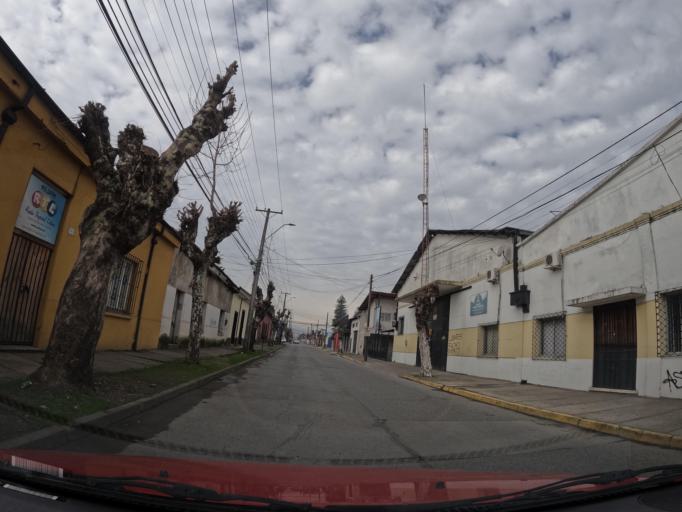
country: CL
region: Maule
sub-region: Provincia de Linares
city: Linares
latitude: -35.8497
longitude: -71.5933
